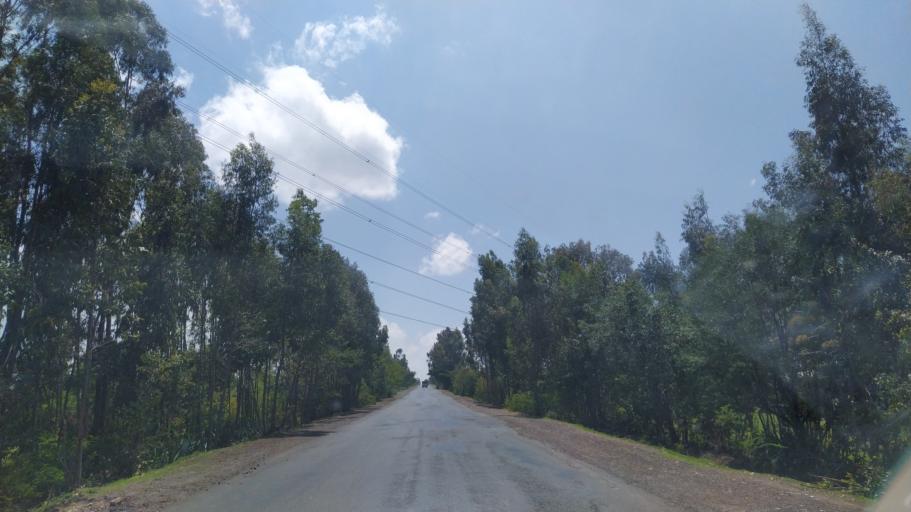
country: ET
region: Southern Nations, Nationalities, and People's Region
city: Butajira
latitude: 7.7545
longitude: 38.1299
